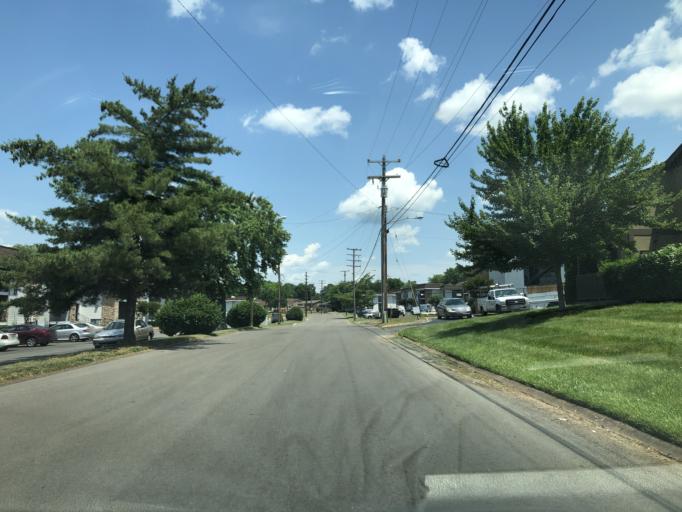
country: US
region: Tennessee
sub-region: Davidson County
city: Goodlettsville
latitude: 36.2682
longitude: -86.7019
